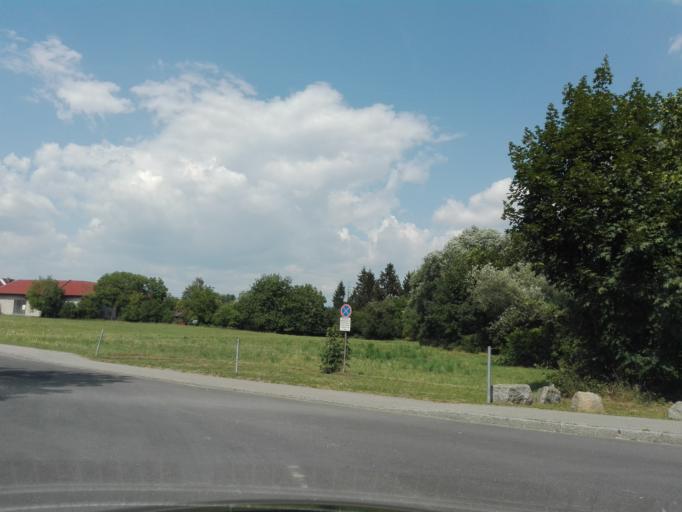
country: AT
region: Upper Austria
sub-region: Politischer Bezirk Linz-Land
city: Traun
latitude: 48.2158
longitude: 14.2237
